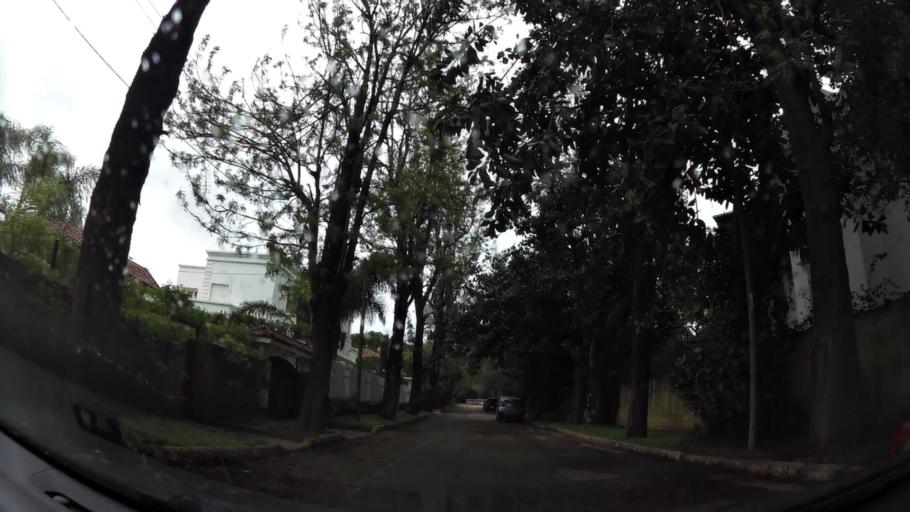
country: MA
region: Grand Casablanca
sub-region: Casablanca
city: Casablanca
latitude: 33.5327
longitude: -7.6290
